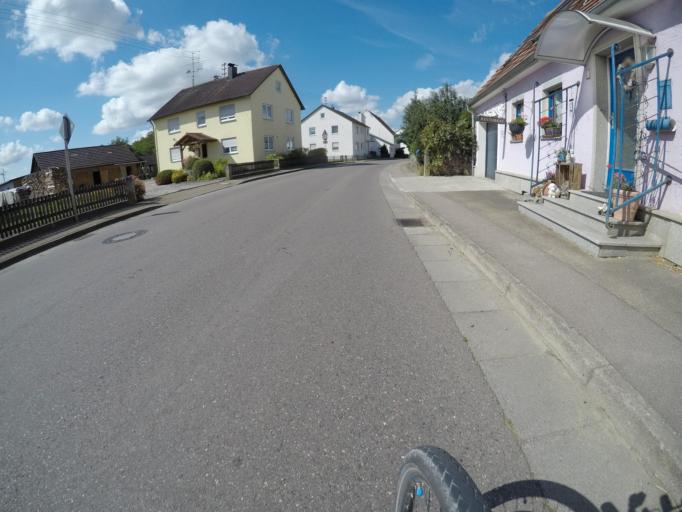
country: DE
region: Bavaria
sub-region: Swabia
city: Finningen
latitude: 48.6229
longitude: 10.5122
